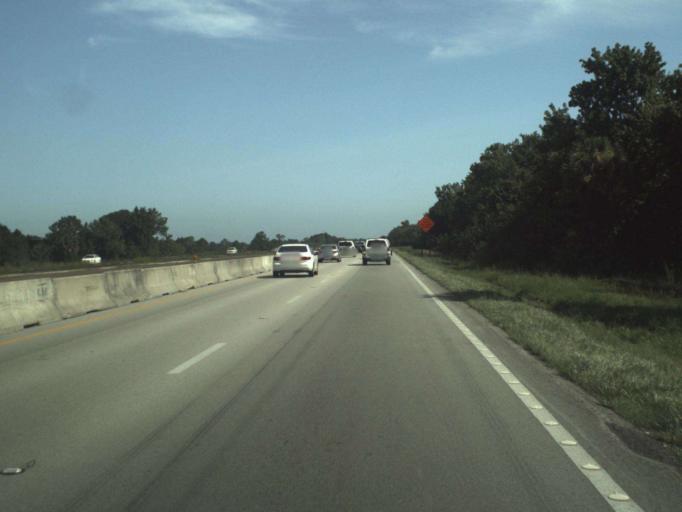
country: US
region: Florida
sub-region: Indian River County
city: Fellsmere
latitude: 27.7277
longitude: -80.5462
